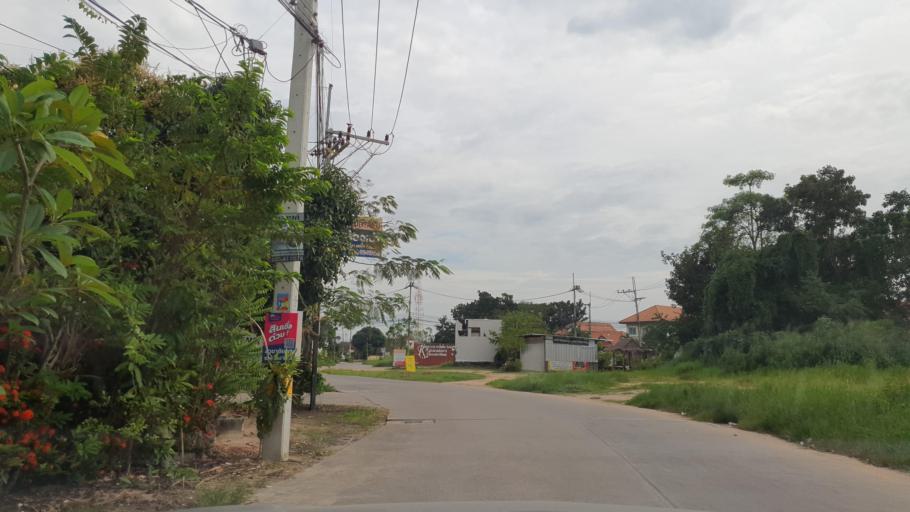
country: TH
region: Chon Buri
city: Phatthaya
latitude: 12.9556
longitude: 100.9188
